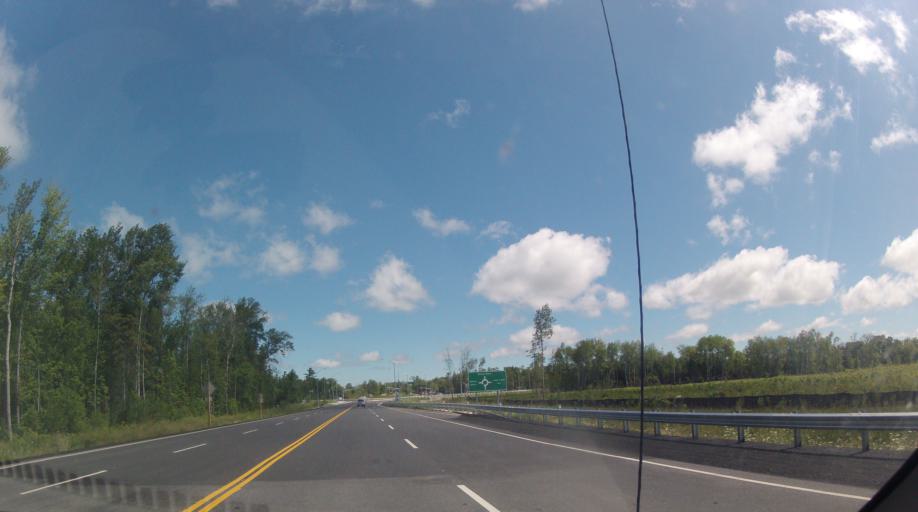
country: CA
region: Ontario
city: Wasaga Beach
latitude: 44.4653
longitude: -80.1098
